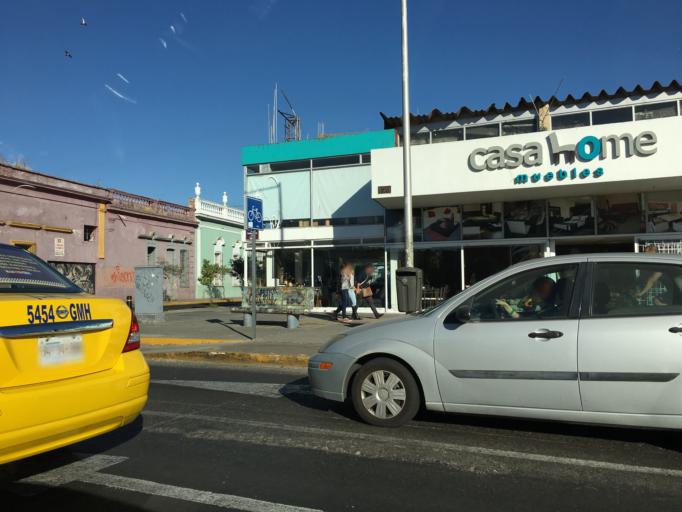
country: MX
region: Jalisco
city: Guadalajara
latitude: 20.6785
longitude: -103.3542
